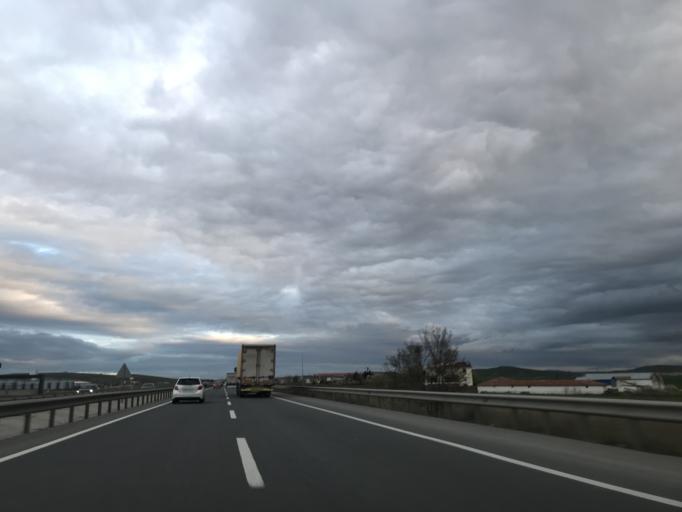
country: TR
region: Ankara
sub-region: Goelbasi
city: Golbasi
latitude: 39.6252
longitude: 32.8380
